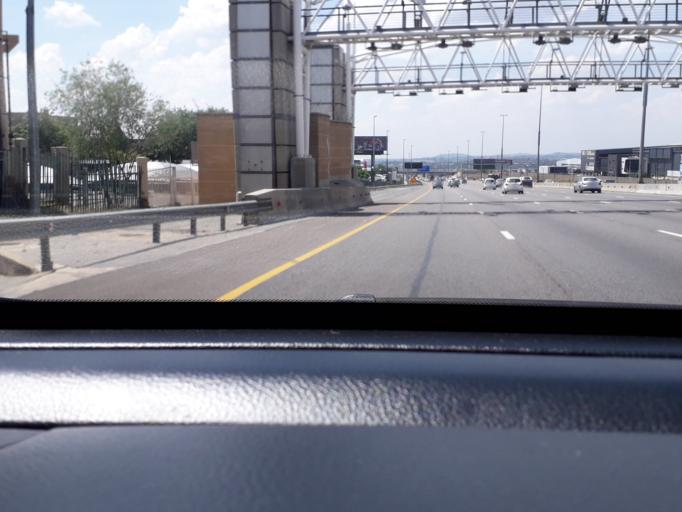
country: ZA
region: Gauteng
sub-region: City of Tshwane Metropolitan Municipality
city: Centurion
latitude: -25.8983
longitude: 28.1631
